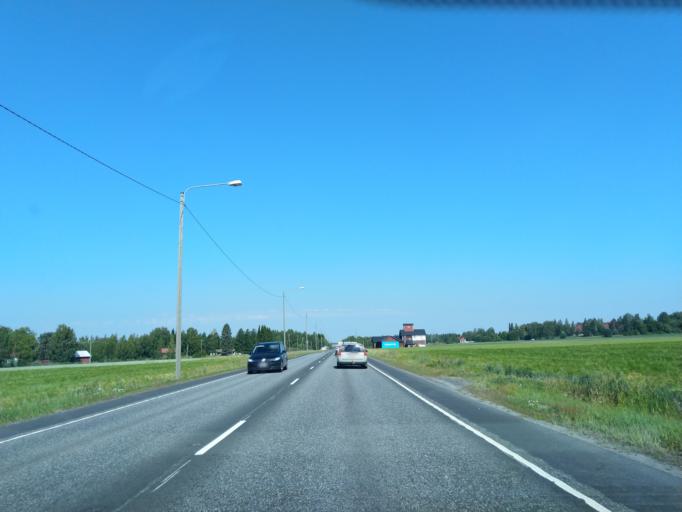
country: FI
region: Satakunta
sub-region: Pori
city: Nakkila
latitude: 61.3551
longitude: 22.0060
